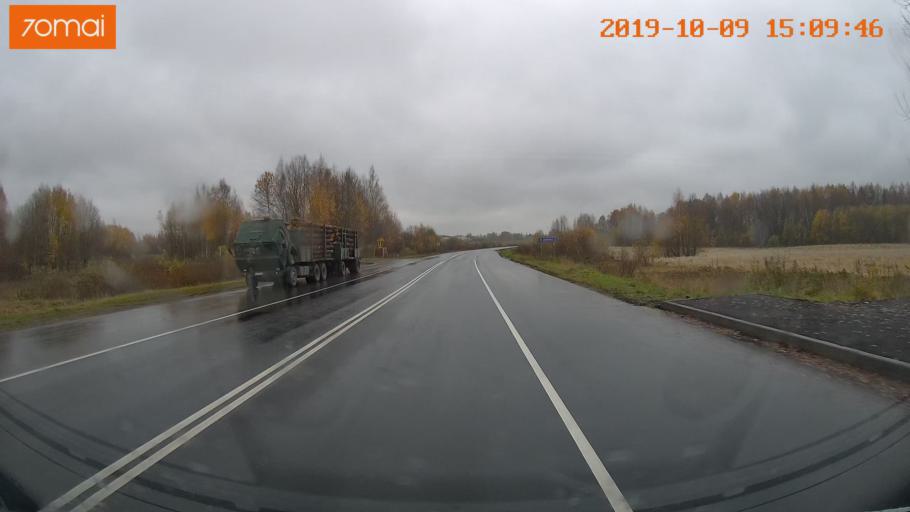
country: RU
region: Kostroma
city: Susanino
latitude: 58.1869
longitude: 41.6486
